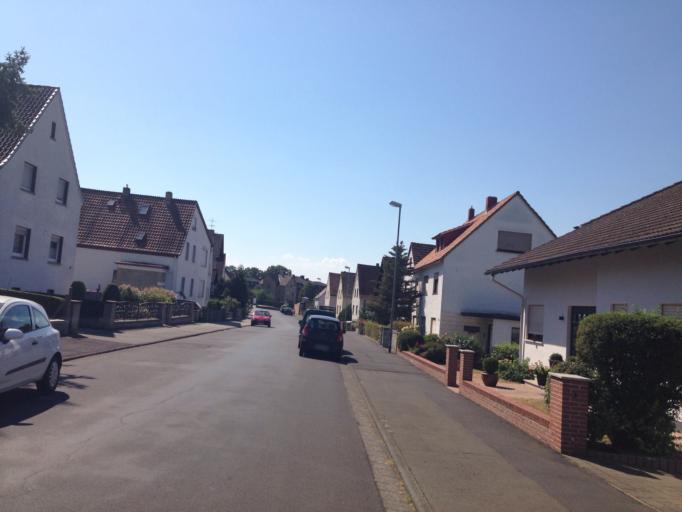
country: DE
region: Hesse
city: Lollar
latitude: 50.6450
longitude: 8.7066
